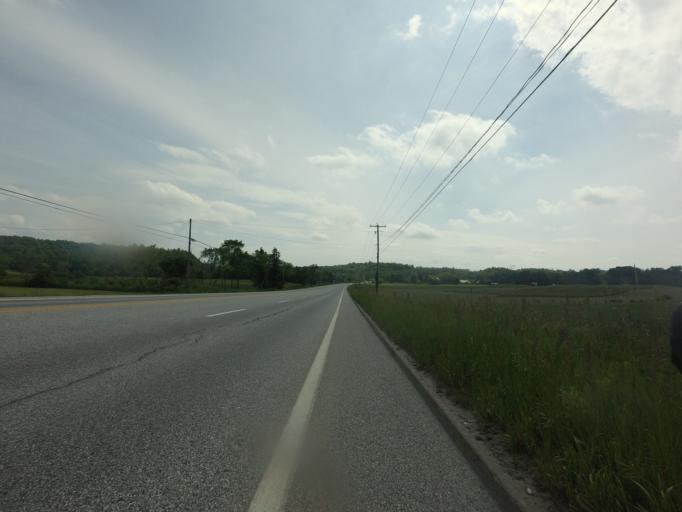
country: CA
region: Quebec
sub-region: Outaouais
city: Wakefield
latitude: 45.7946
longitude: -75.9473
